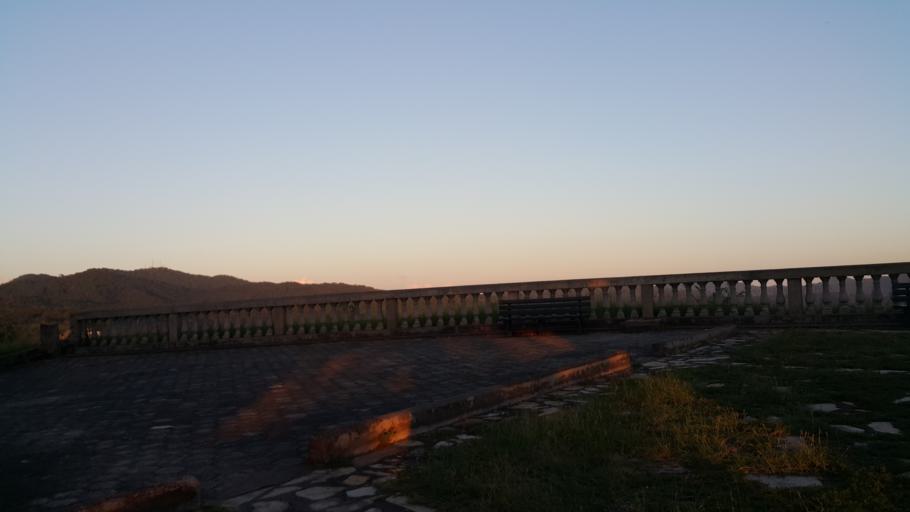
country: NI
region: Rivas
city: San Juan del Sur
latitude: 11.2618
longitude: -85.8819
